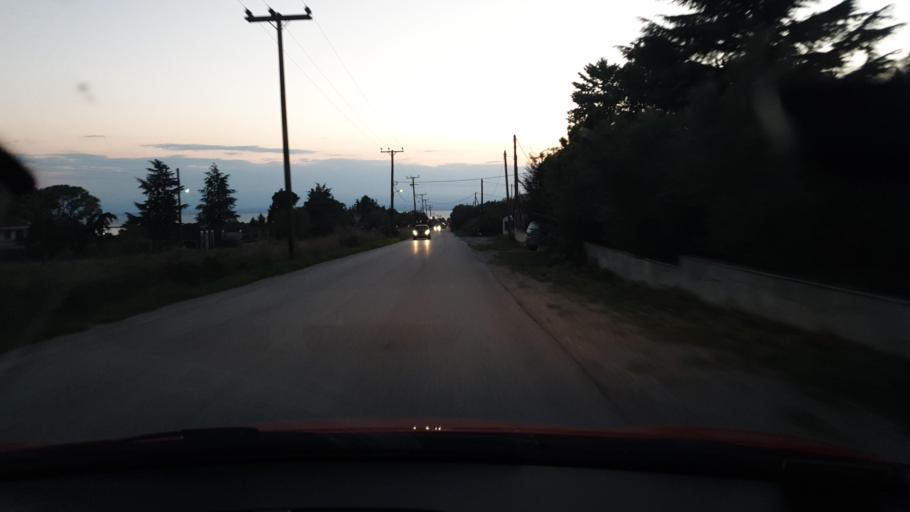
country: GR
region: Central Macedonia
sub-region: Nomos Thessalonikis
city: Agia Triada
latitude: 40.4972
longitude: 22.8433
